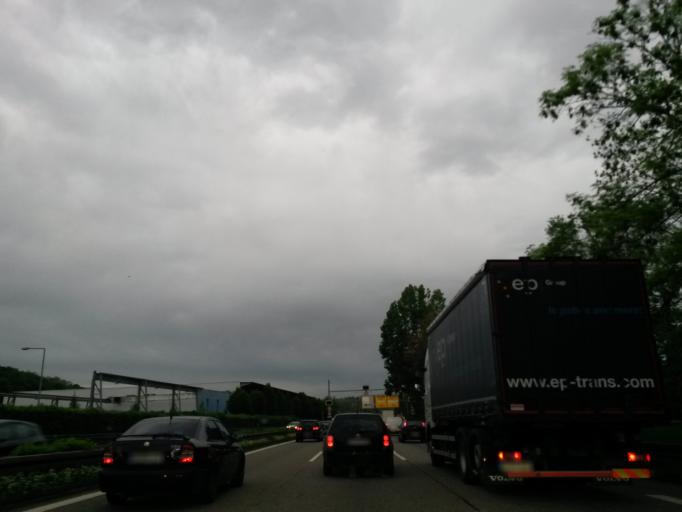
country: DE
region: Baden-Wuerttemberg
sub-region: Regierungsbezirk Stuttgart
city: Stuttgart-Ost
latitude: 48.7916
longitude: 9.2186
